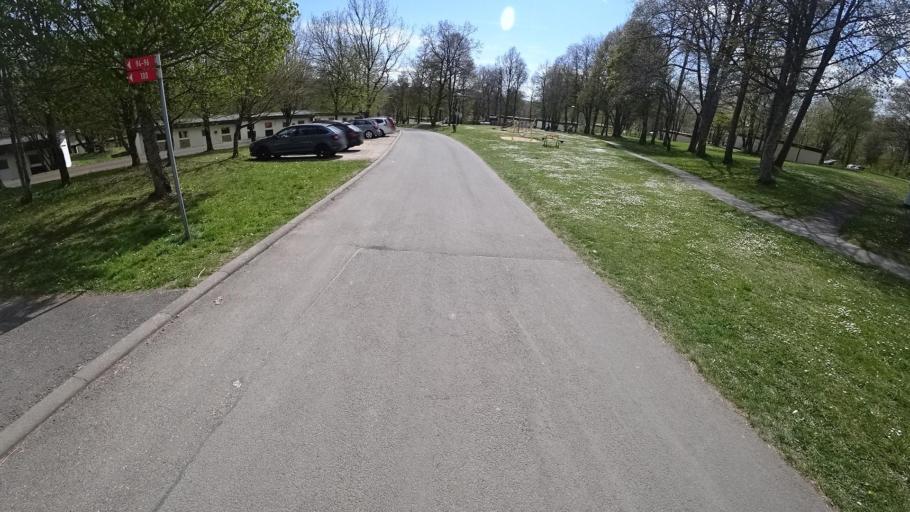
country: DE
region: Rheinland-Pfalz
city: Kell am See
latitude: 49.6475
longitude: 6.8108
